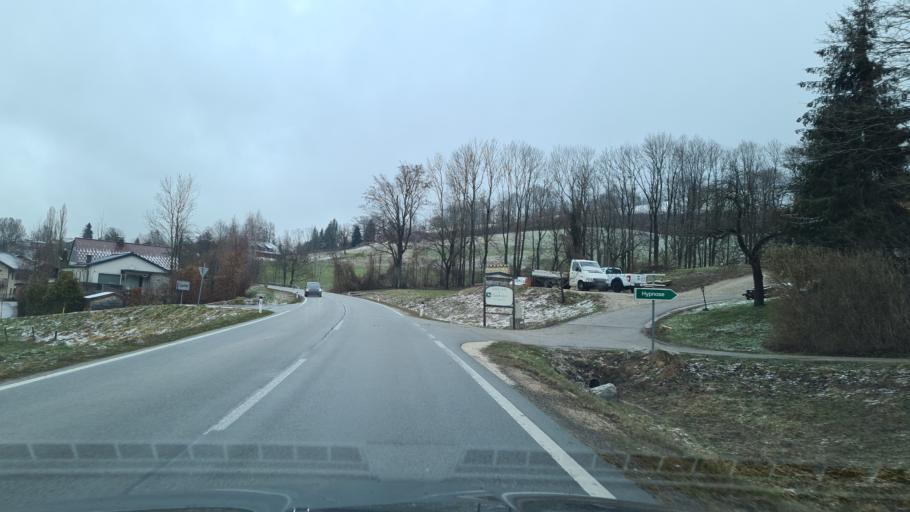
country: AT
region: Upper Austria
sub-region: Politischer Bezirk Vocklabruck
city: Oberhofen am Irrsee
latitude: 47.9300
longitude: 13.3129
